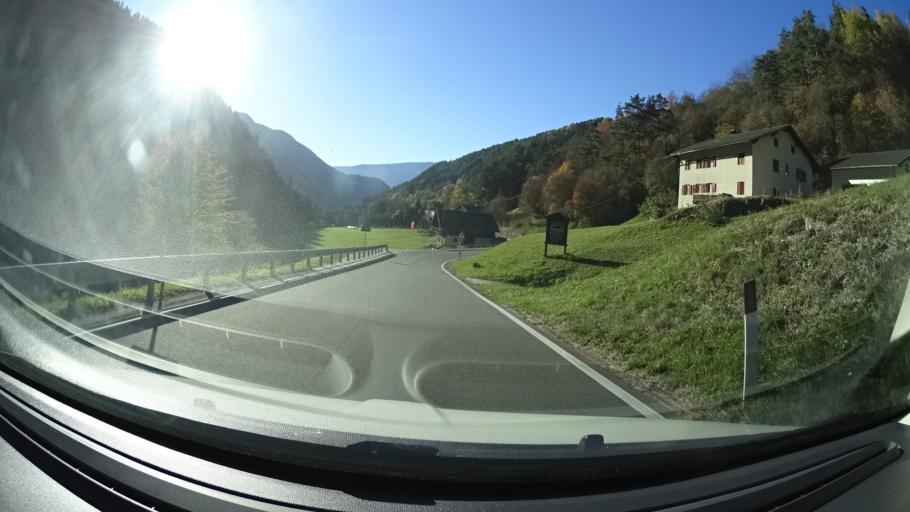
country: IT
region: Trentino-Alto Adige
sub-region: Bolzano
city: Laion
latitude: 46.5971
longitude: 11.6034
